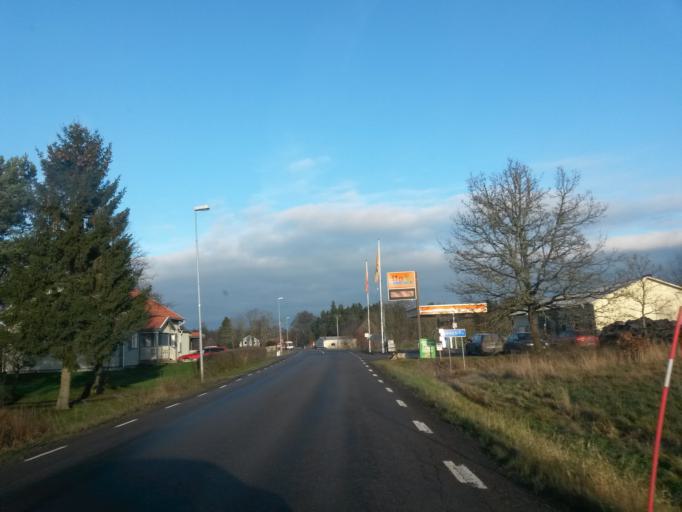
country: SE
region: Vaestra Goetaland
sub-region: Essunga Kommun
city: Nossebro
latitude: 58.2268
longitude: 12.7204
